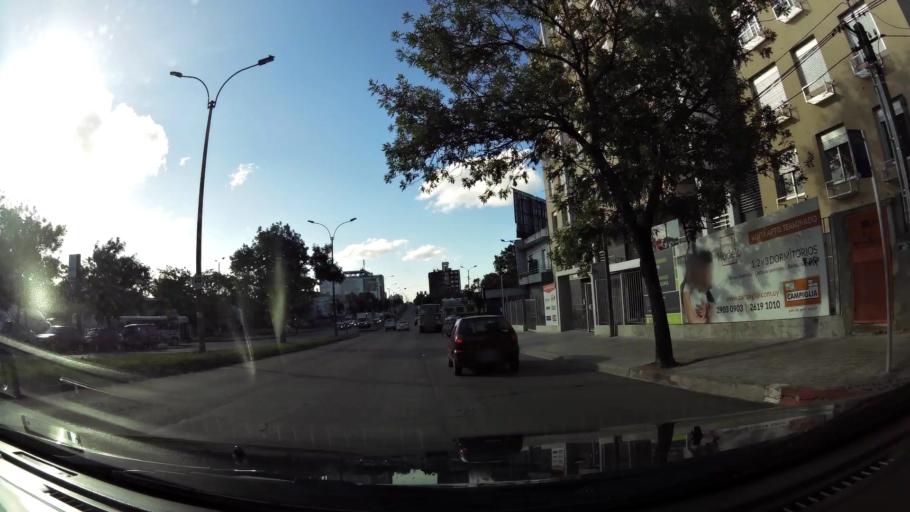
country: UY
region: Montevideo
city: Montevideo
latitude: -34.8764
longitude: -56.1517
